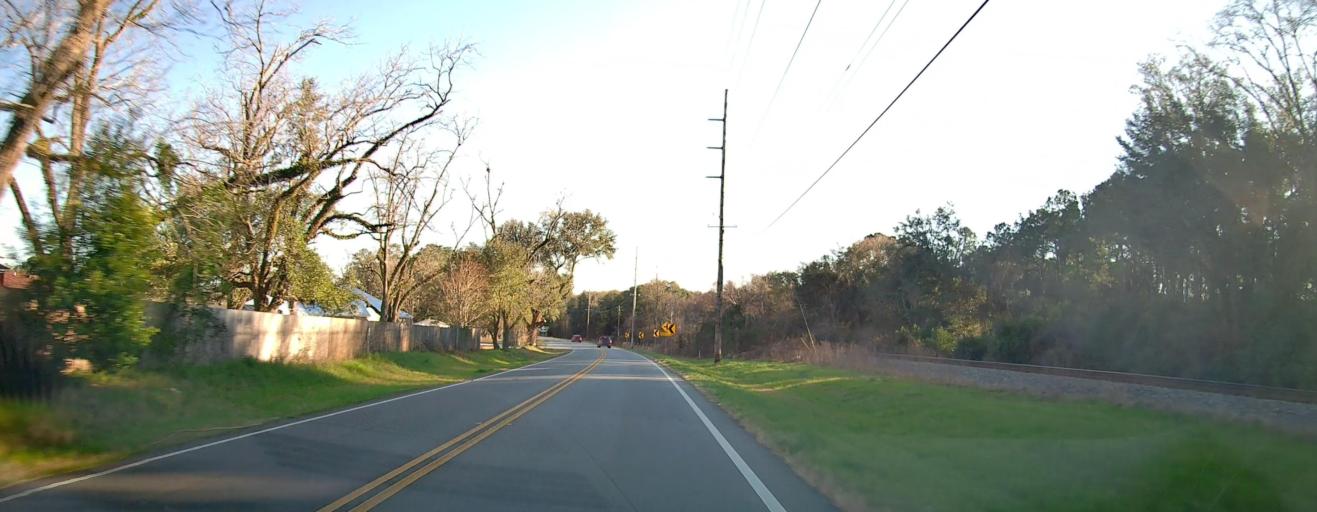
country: US
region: Georgia
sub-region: Dougherty County
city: Albany
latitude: 31.6246
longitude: -84.1634
